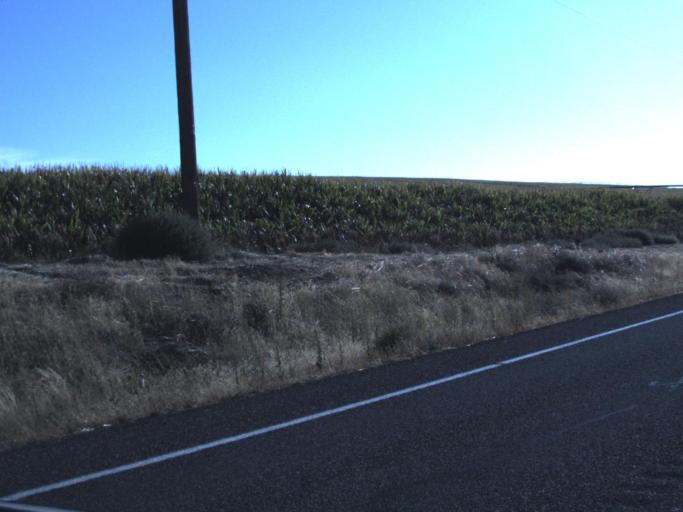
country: US
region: Washington
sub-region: Walla Walla County
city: Burbank
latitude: 46.2620
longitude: -118.7882
